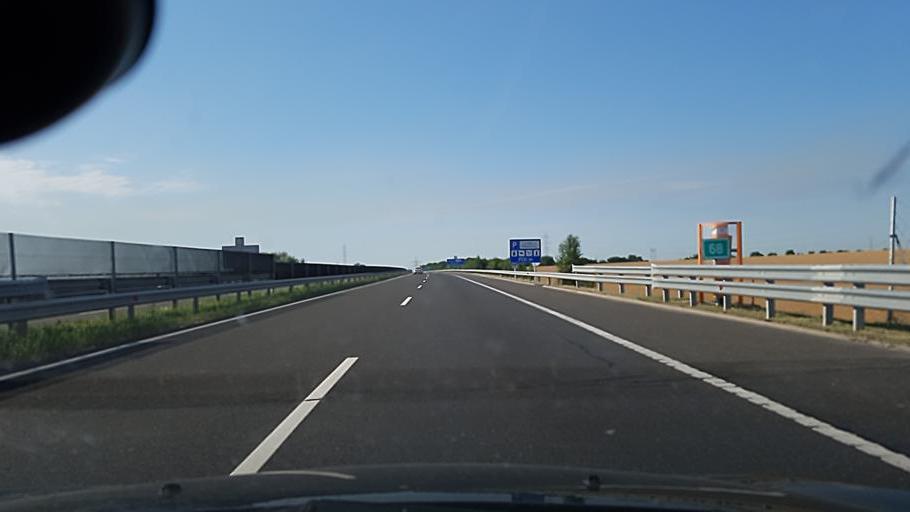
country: HU
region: Fejer
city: dunaujvaros
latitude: 46.9826
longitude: 18.8850
